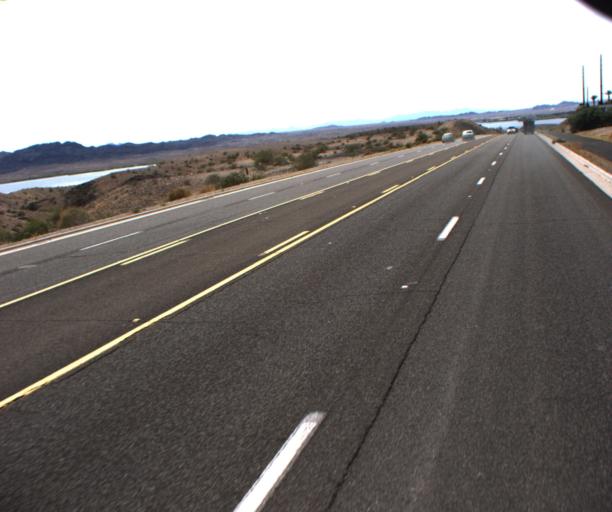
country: US
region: Arizona
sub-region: Mohave County
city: Lake Havasu City
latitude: 34.4525
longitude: -114.3150
